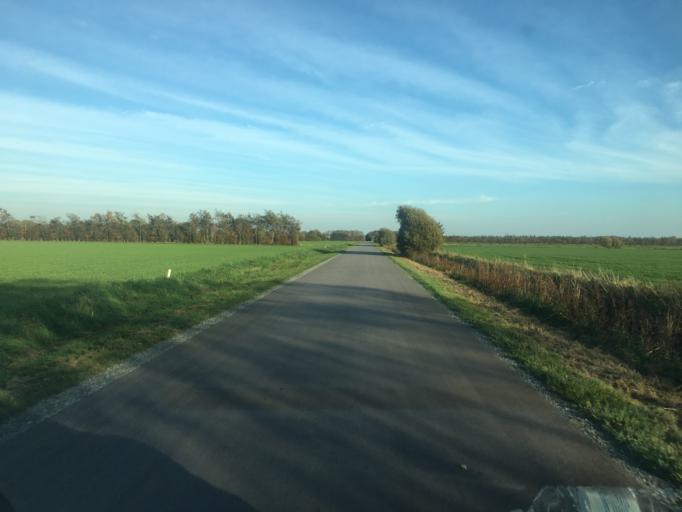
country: DE
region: Schleswig-Holstein
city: Bramstedtlund
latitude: 54.8947
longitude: 9.0436
